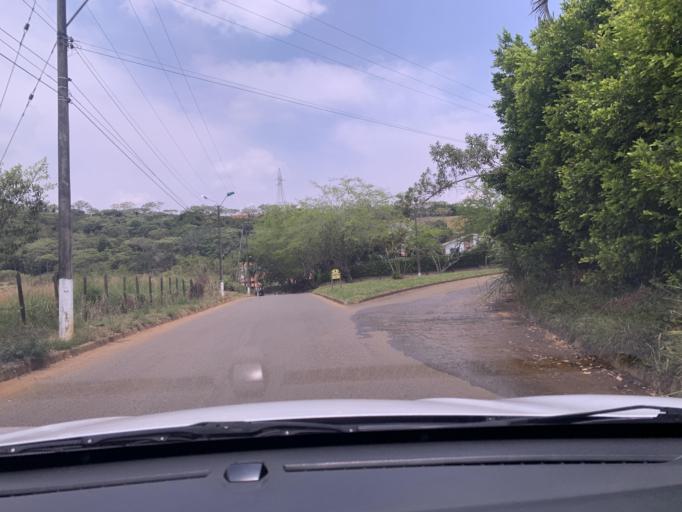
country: CO
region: Valle del Cauca
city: Jamundi
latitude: 3.3383
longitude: -76.5532
